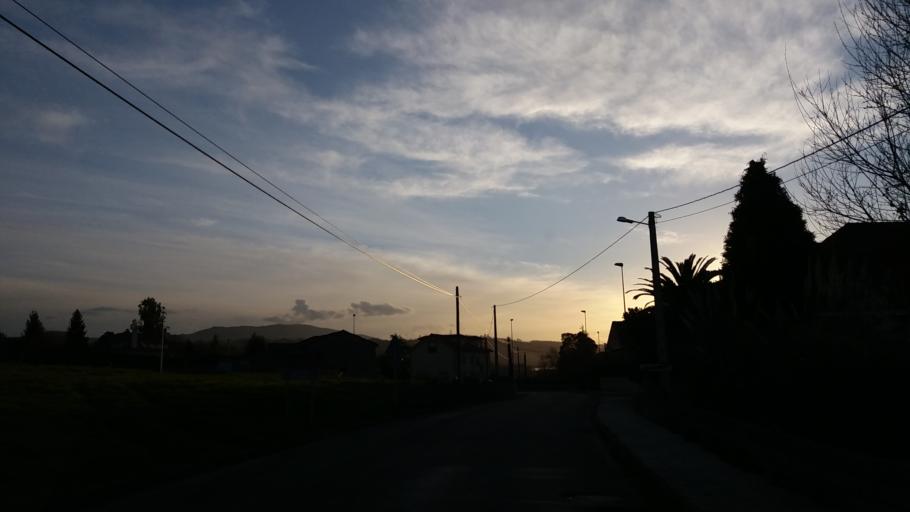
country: ES
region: Cantabria
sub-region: Provincia de Cantabria
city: Reocin
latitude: 43.3639
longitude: -4.0818
